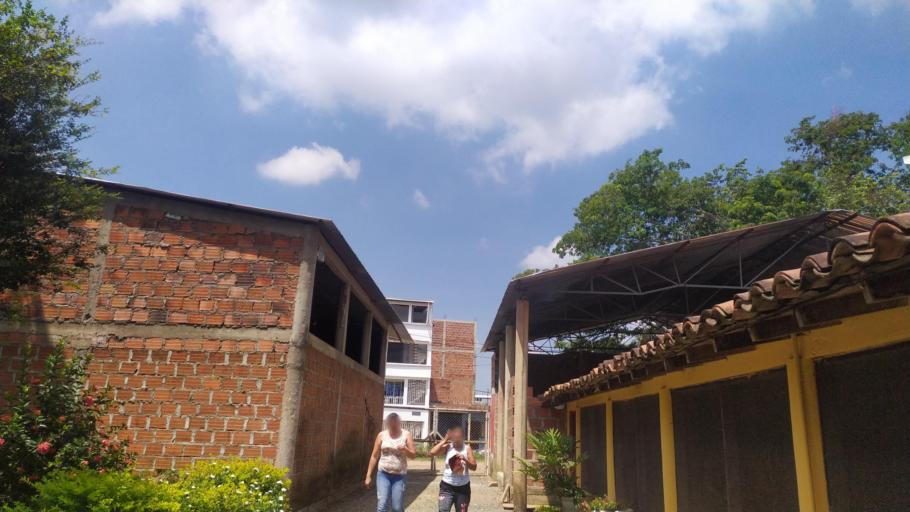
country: CO
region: Valle del Cauca
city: Jamundi
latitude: 3.2481
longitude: -76.5423
